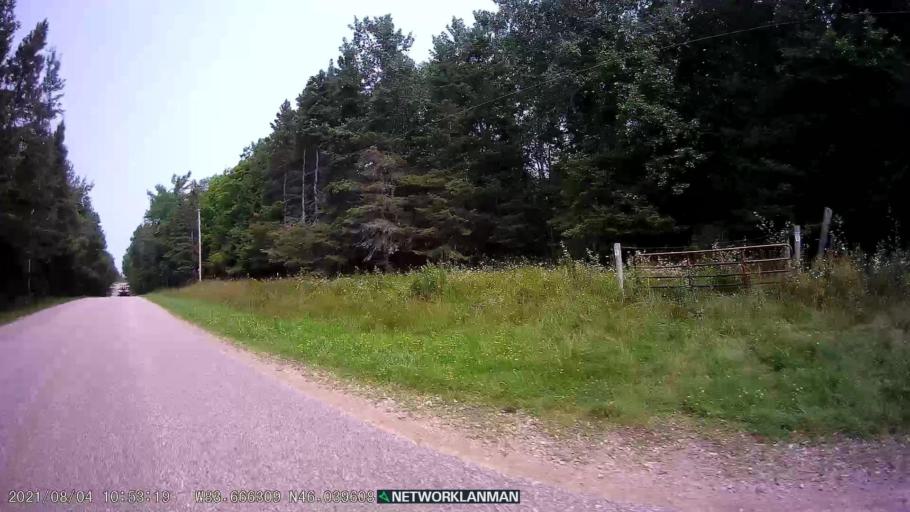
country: CA
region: Ontario
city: Thessalon
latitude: 46.0405
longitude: -83.6663
